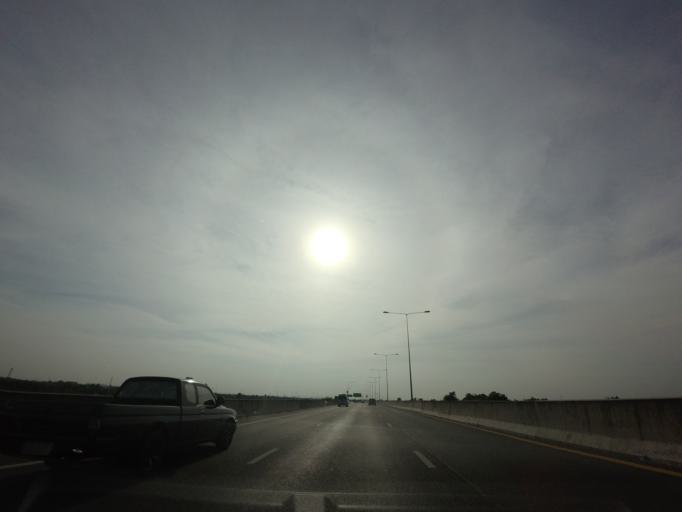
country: TH
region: Bangkok
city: Sai Mai
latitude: 13.8924
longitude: 100.6588
